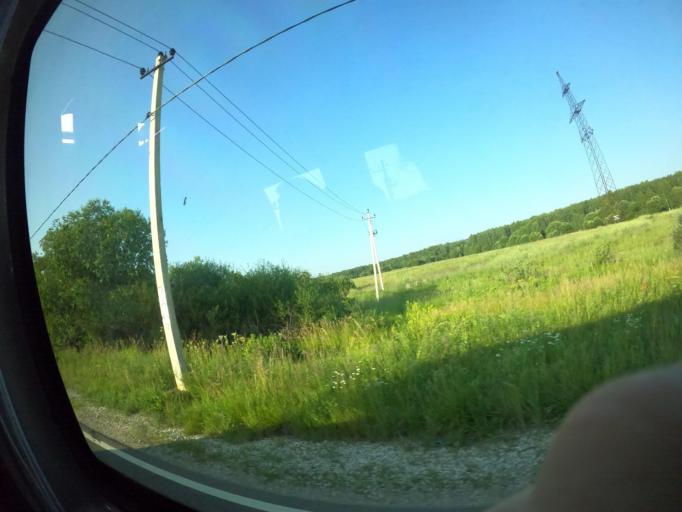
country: RU
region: Moskovskaya
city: Obolensk
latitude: 54.9315
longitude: 37.2516
